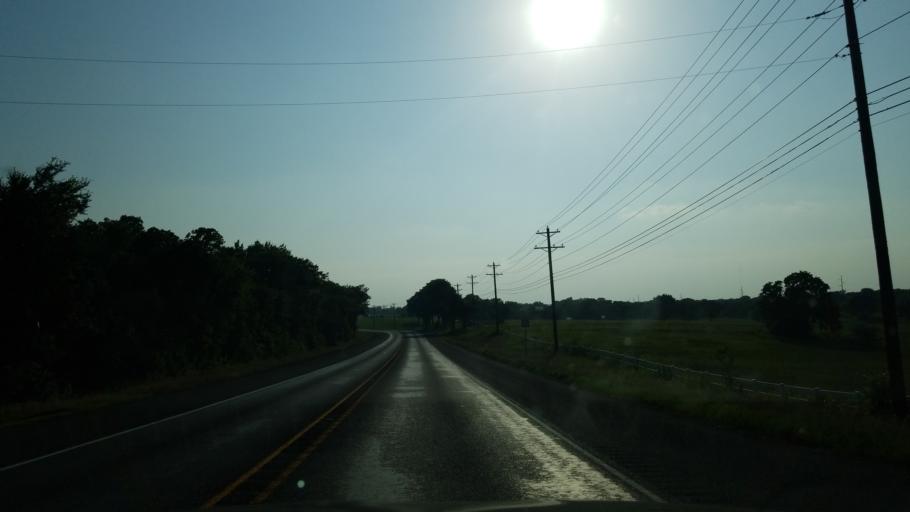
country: US
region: Texas
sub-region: Denton County
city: Aubrey
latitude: 33.3047
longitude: -97.0070
